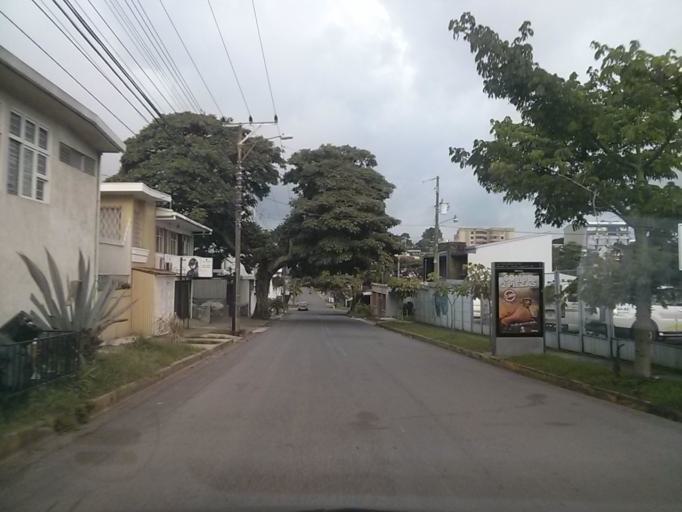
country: CR
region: San Jose
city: San Pedro
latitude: 9.9301
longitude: -84.0597
